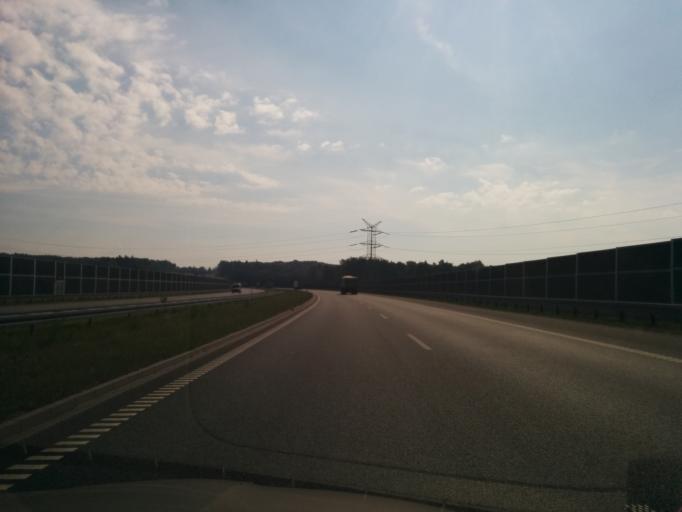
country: PL
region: Silesian Voivodeship
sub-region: Powiat tarnogorski
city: Wieszowa
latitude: 50.3845
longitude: 18.8234
